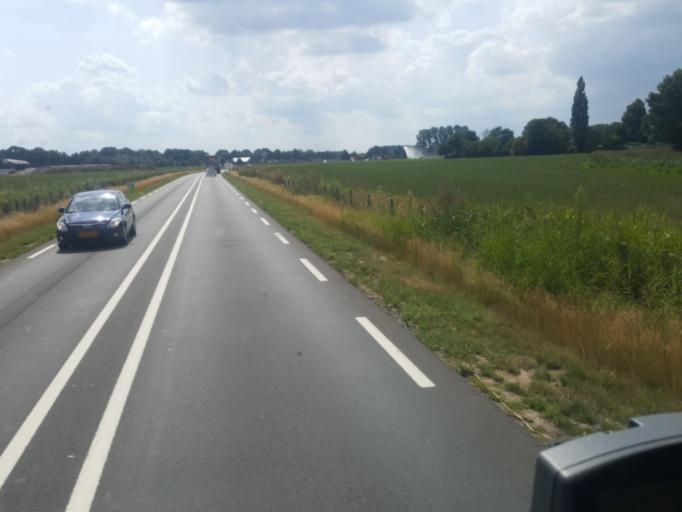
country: NL
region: North Brabant
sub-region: Gemeente Cuijk
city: Cuijk
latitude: 51.6865
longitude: 5.8734
